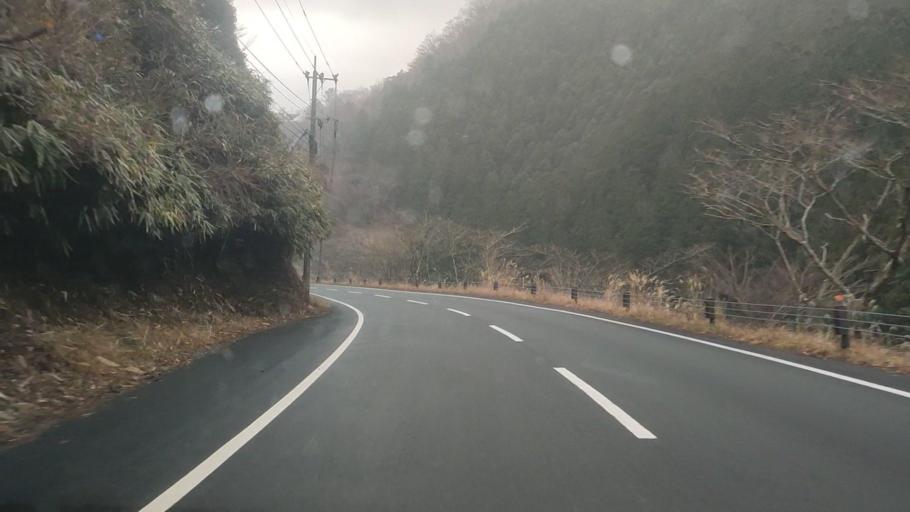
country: JP
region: Kumamoto
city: Matsubase
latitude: 32.5502
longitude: 130.9344
